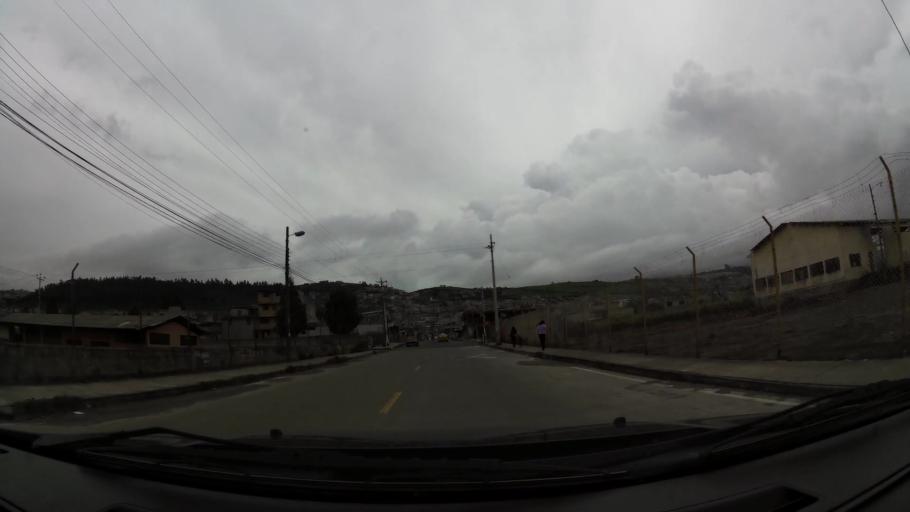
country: EC
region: Pichincha
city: Sangolqui
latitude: -0.3186
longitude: -78.5389
